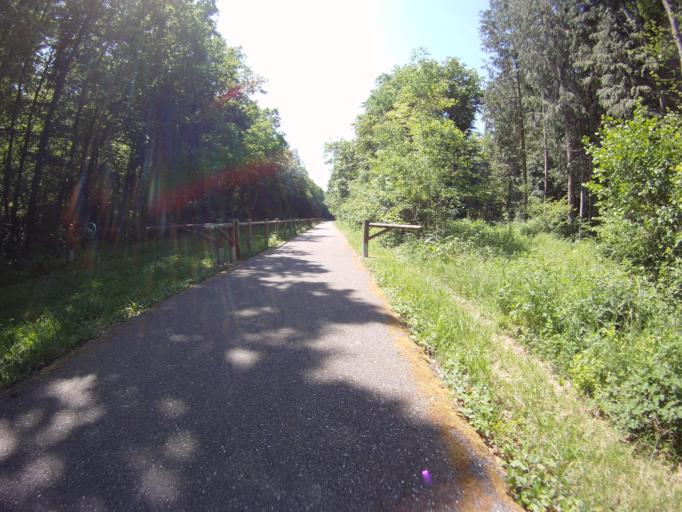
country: FR
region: Lorraine
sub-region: Departement de Meurthe-et-Moselle
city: Champenoux
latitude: 48.7493
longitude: 6.3235
